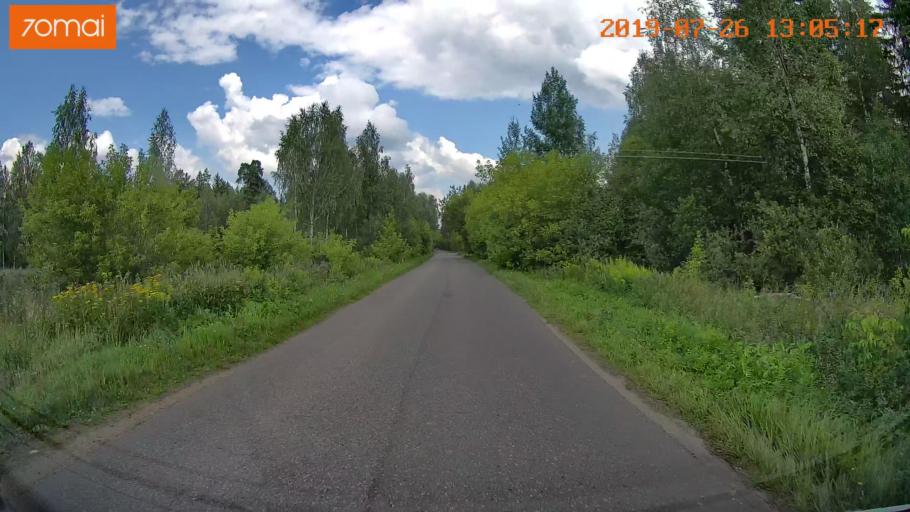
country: RU
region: Ivanovo
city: Bogorodskoye
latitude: 57.0608
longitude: 41.0334
